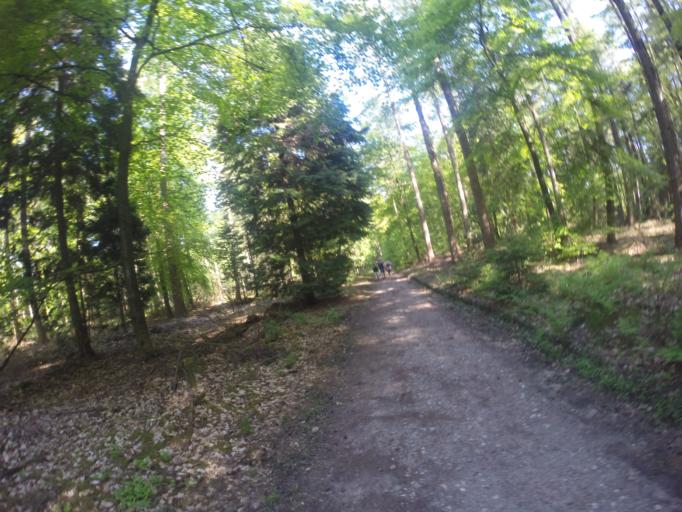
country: NL
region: Gelderland
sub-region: Gemeente Montferland
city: s-Heerenberg
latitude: 51.9080
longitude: 6.2148
